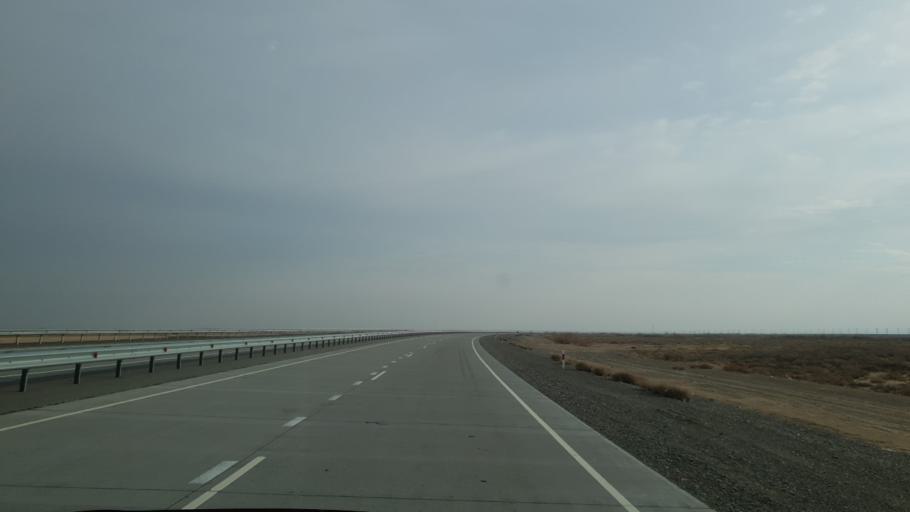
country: KZ
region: Almaty Oblysy
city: Kegen
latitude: 43.7736
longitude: 79.1630
